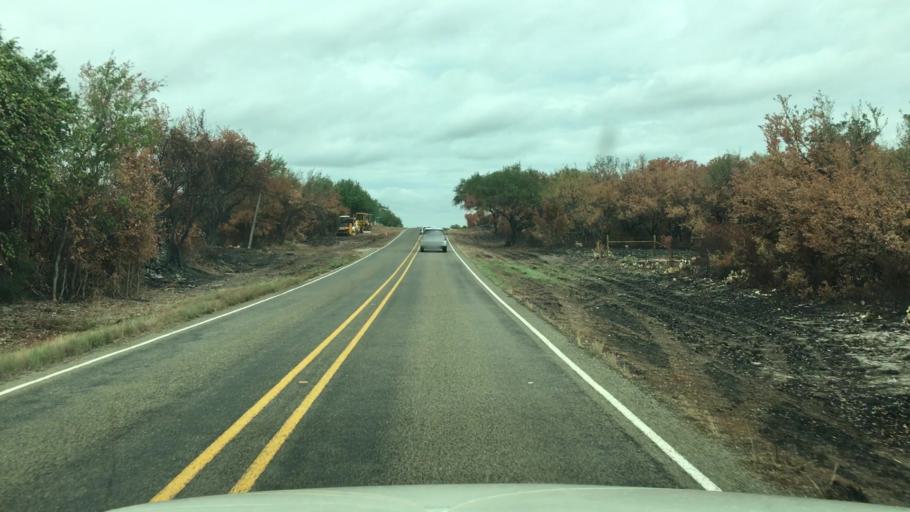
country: US
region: Texas
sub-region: Llano County
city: Horseshoe Bay
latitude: 30.4812
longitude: -98.4239
